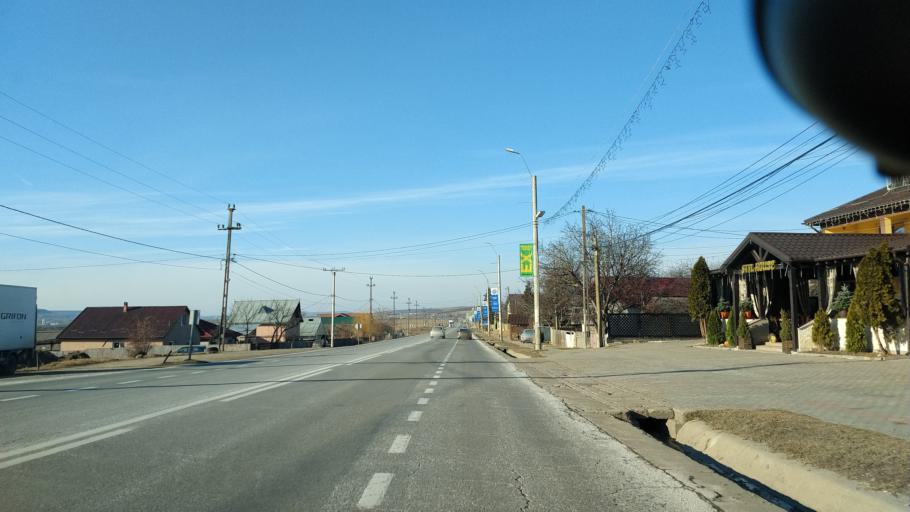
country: RO
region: Iasi
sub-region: Comuna Letcani
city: Letcani
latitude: 47.1962
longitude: 27.3978
